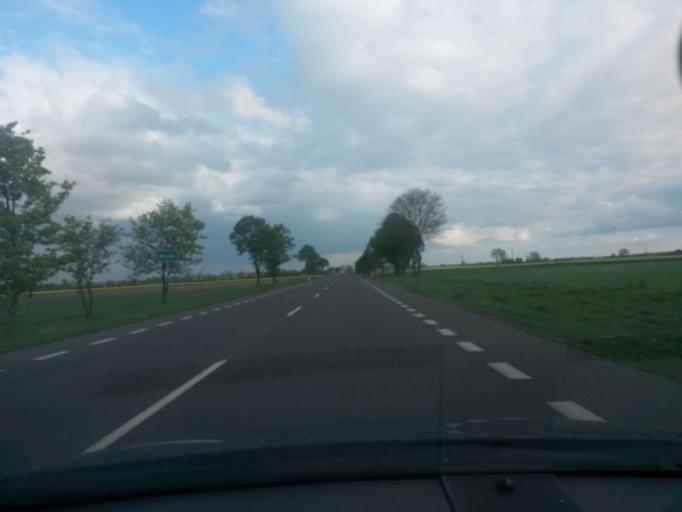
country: PL
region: Masovian Voivodeship
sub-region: Powiat plocki
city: Drobin
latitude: 52.7310
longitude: 20.0030
